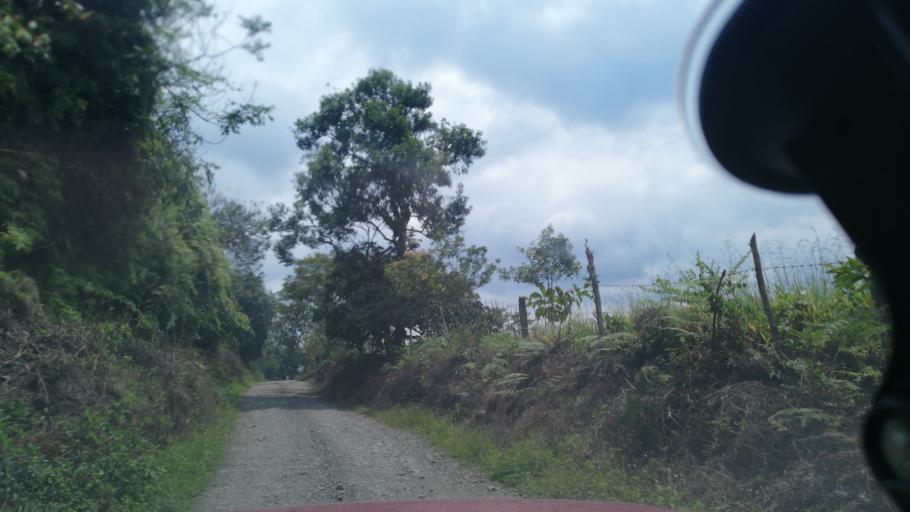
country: CO
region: Cundinamarca
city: Vergara
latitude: 5.1827
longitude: -74.2724
